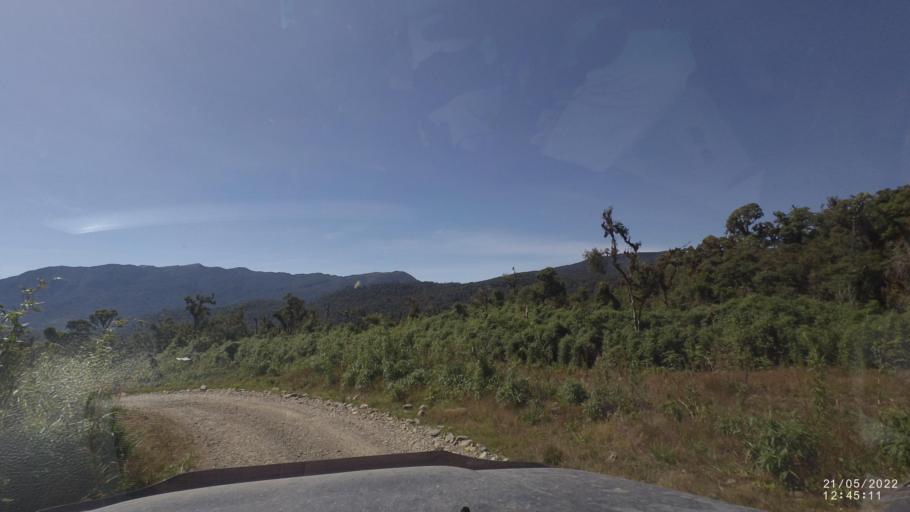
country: BO
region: Cochabamba
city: Colomi
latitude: -17.1882
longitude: -65.9354
